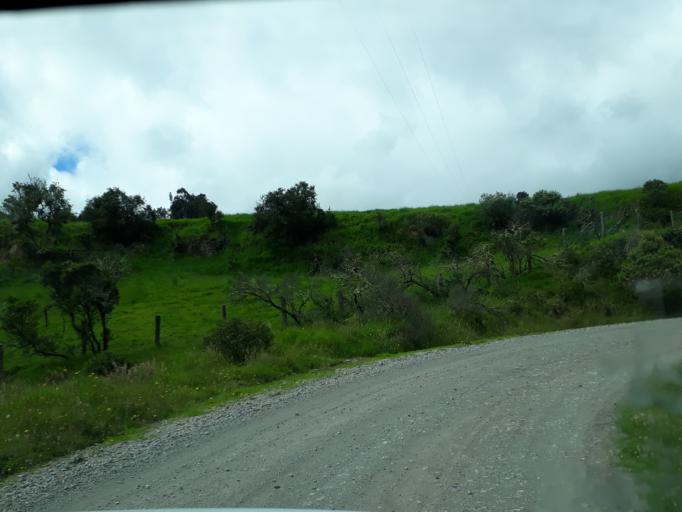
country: CO
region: Cundinamarca
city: La Mesa
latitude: 5.2851
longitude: -73.9076
